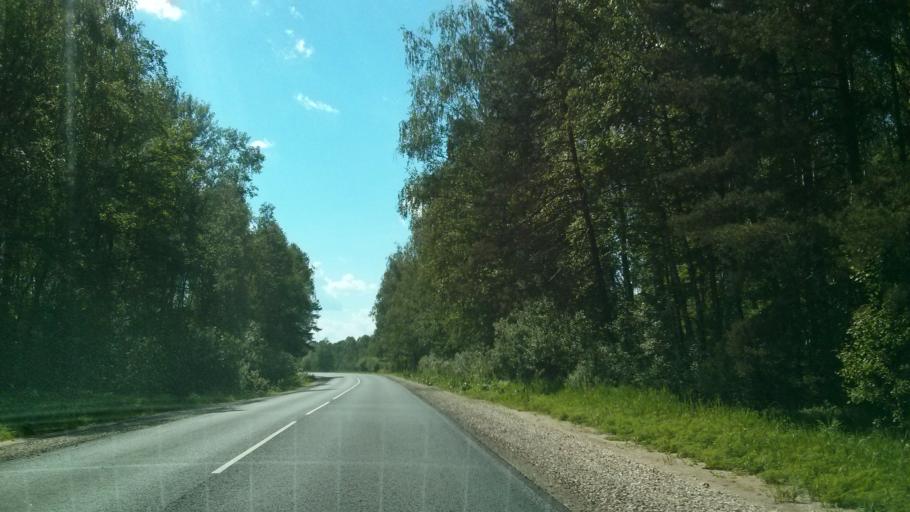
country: RU
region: Vladimir
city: Murom
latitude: 55.5205
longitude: 41.9388
